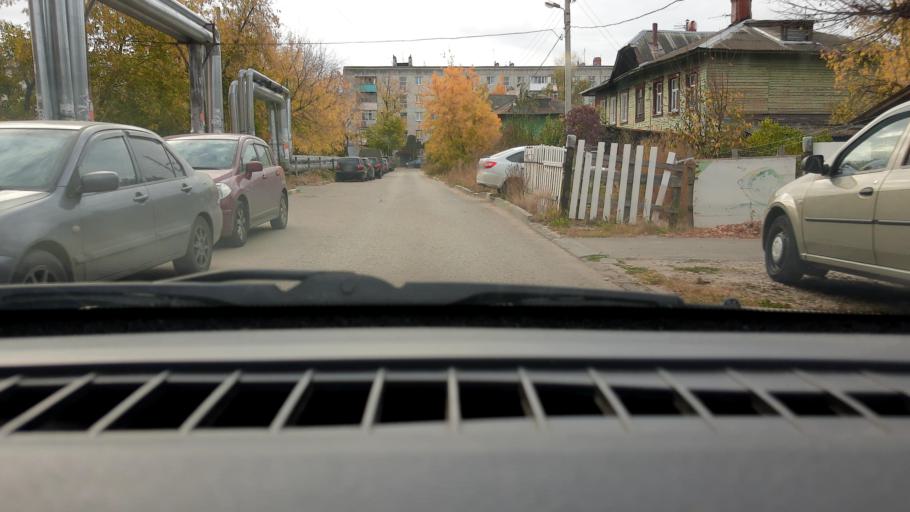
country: RU
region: Nizjnij Novgorod
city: Nizhniy Novgorod
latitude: 56.3009
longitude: 43.9357
